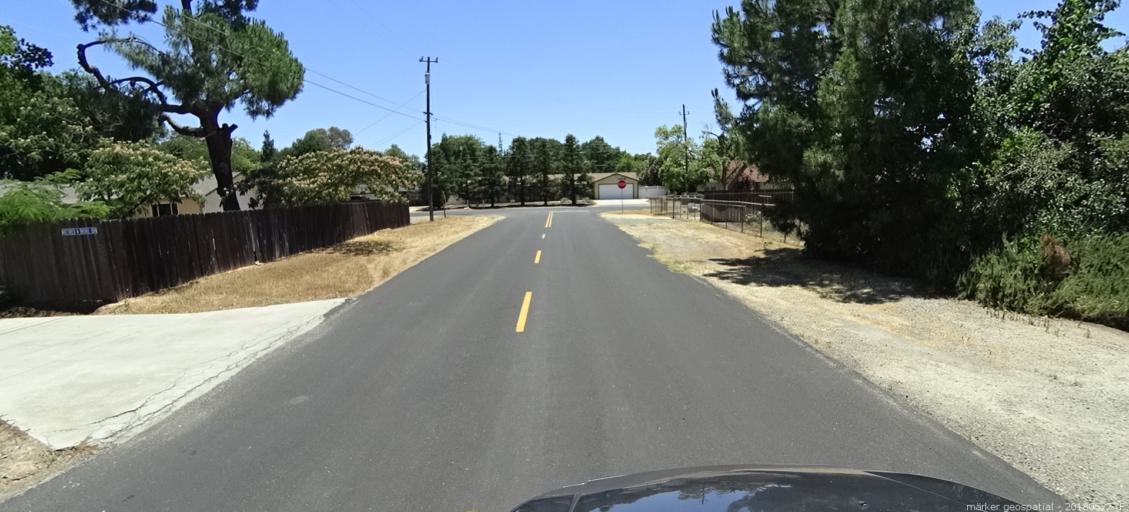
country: US
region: California
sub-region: Madera County
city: Bonadelle Ranchos-Madera Ranchos
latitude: 36.9254
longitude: -119.8838
